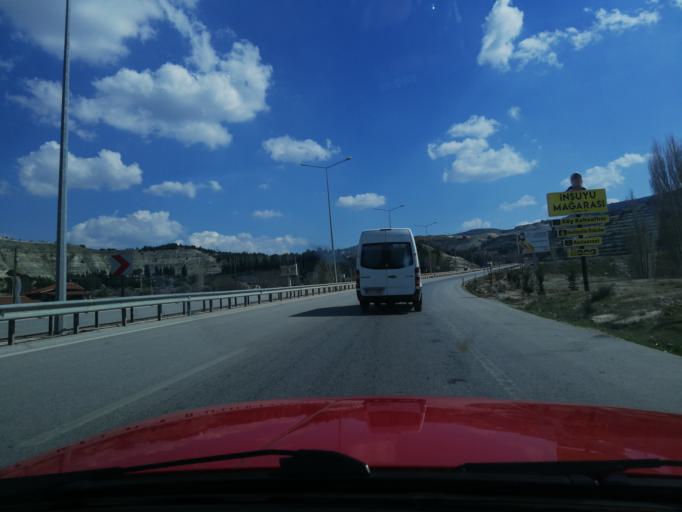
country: TR
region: Burdur
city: Burdur
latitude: 37.7072
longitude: 30.3053
